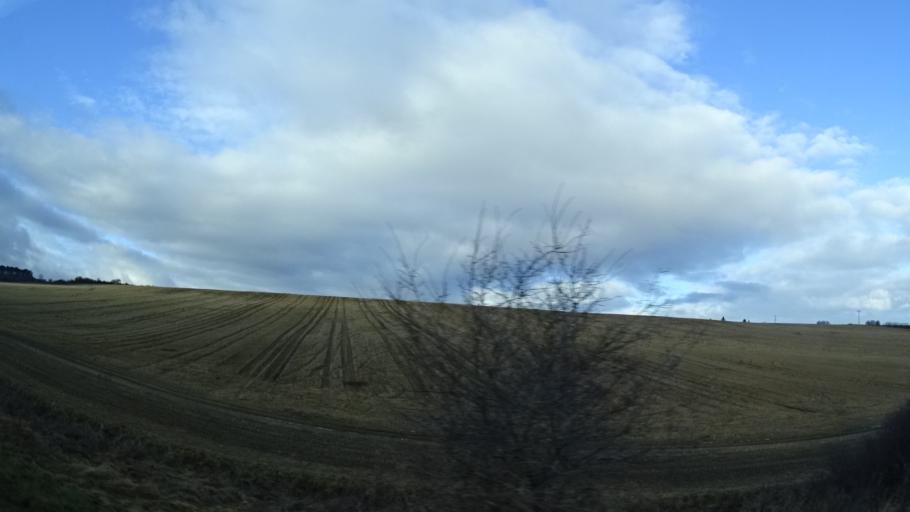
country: DE
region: Thuringia
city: Gossel
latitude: 50.7969
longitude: 10.8350
